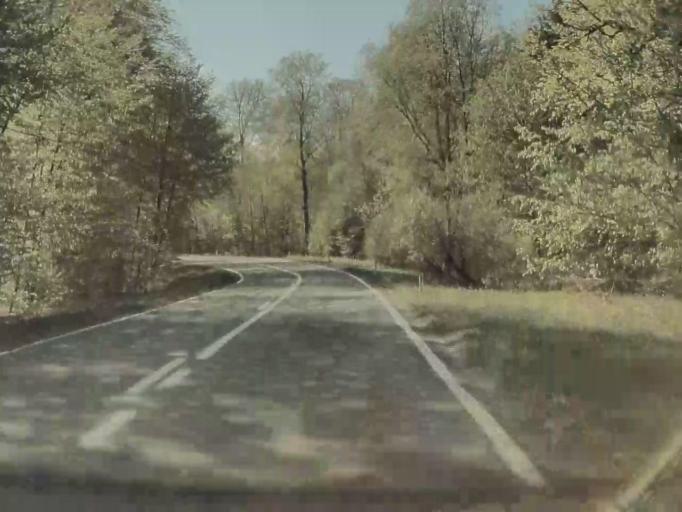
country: BE
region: Wallonia
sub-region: Province du Luxembourg
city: Tellin
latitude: 50.0217
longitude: 5.2026
